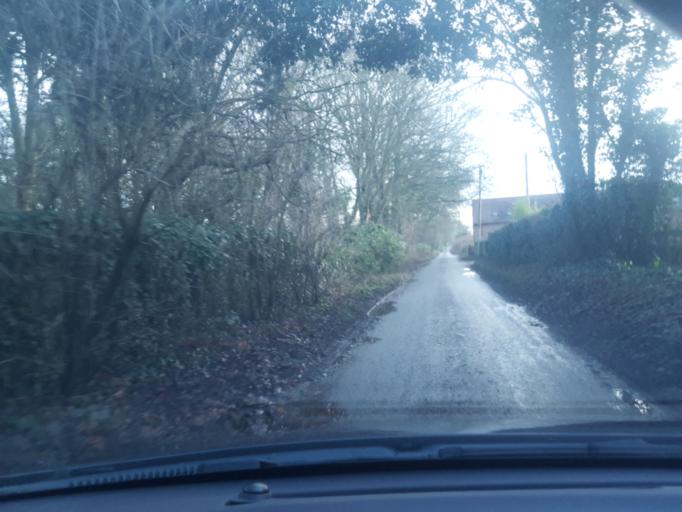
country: GB
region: England
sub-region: Shropshire
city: Tong
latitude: 52.6531
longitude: -2.3141
